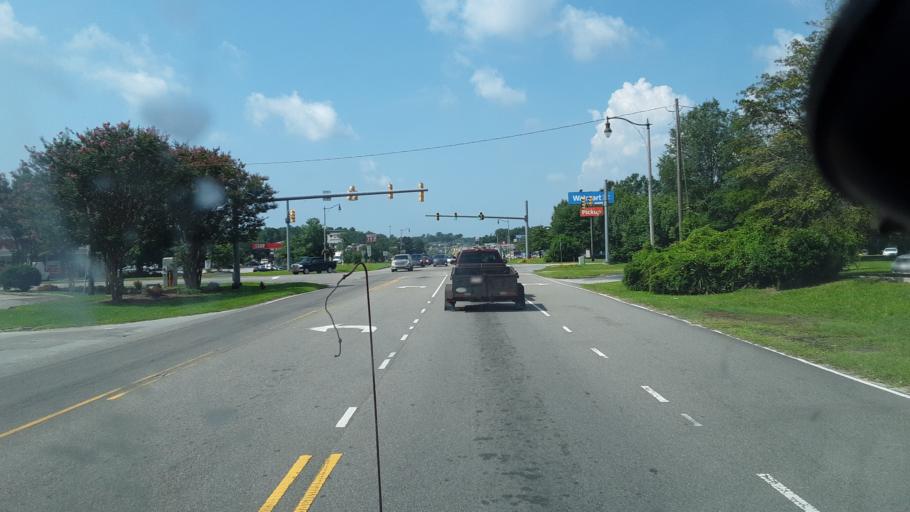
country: US
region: North Carolina
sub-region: Brunswick County
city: Shallotte
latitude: 33.9820
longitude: -78.3727
